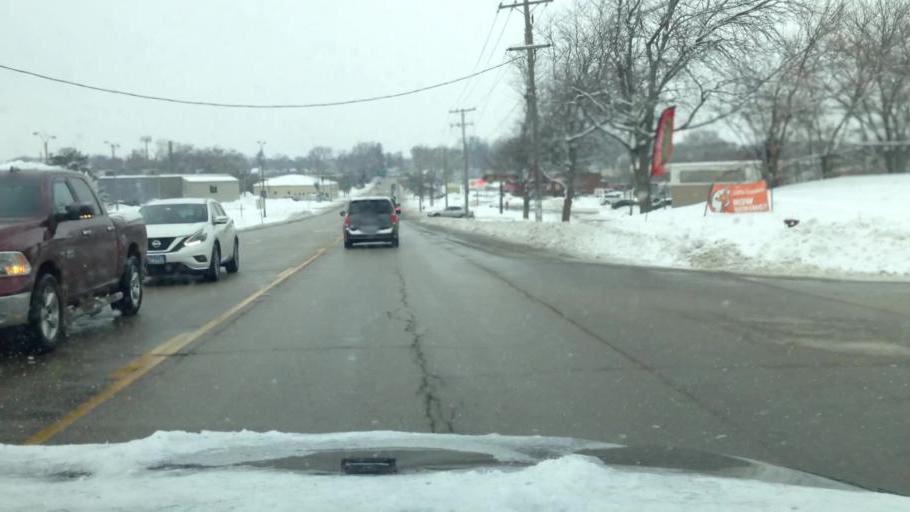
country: US
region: Illinois
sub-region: McHenry County
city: Woodstock
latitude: 42.3144
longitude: -88.4361
